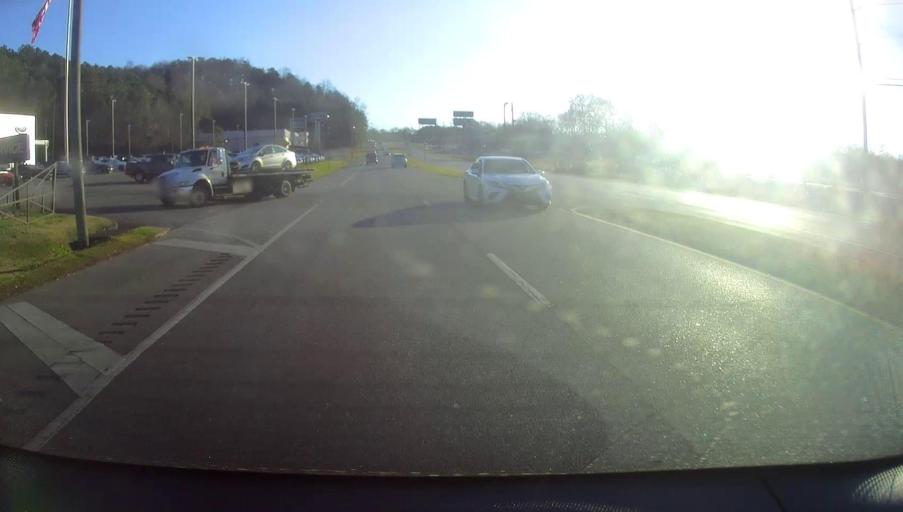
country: US
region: Alabama
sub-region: Calhoun County
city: Oxford
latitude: 33.6282
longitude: -85.8268
